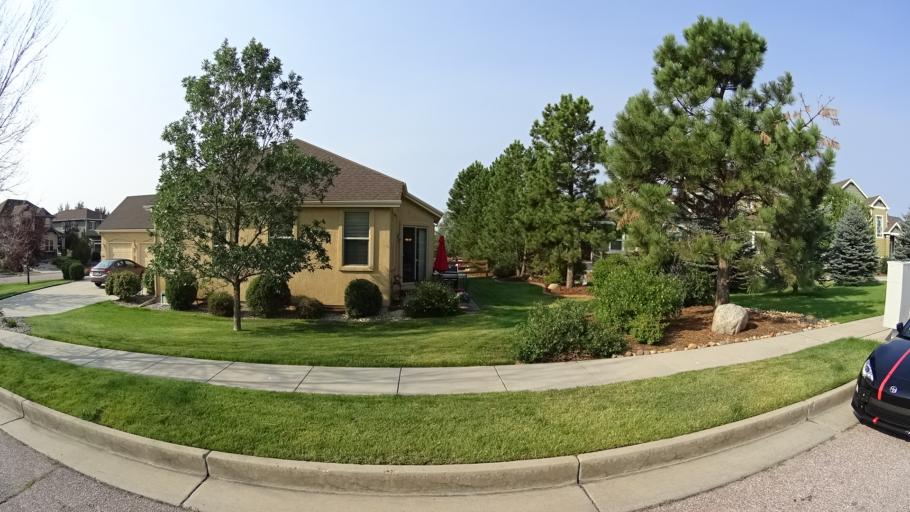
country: US
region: Colorado
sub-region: El Paso County
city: Black Forest
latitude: 38.9569
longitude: -104.7228
